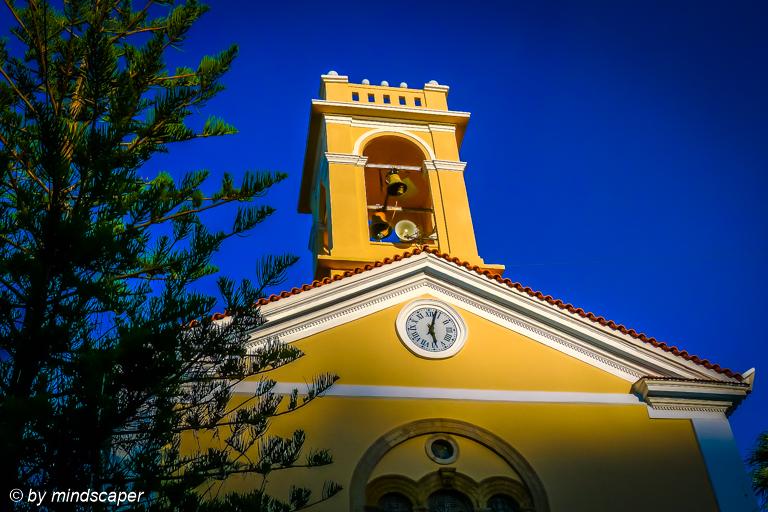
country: GR
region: Peloponnese
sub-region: Nomos Messinias
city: Koroni
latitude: 36.7968
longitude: 21.9571
